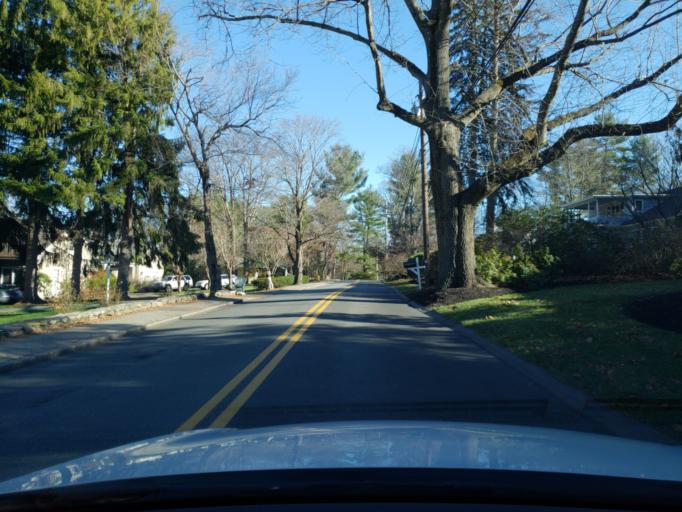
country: US
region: Massachusetts
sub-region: Essex County
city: Andover
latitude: 42.6580
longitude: -71.1218
